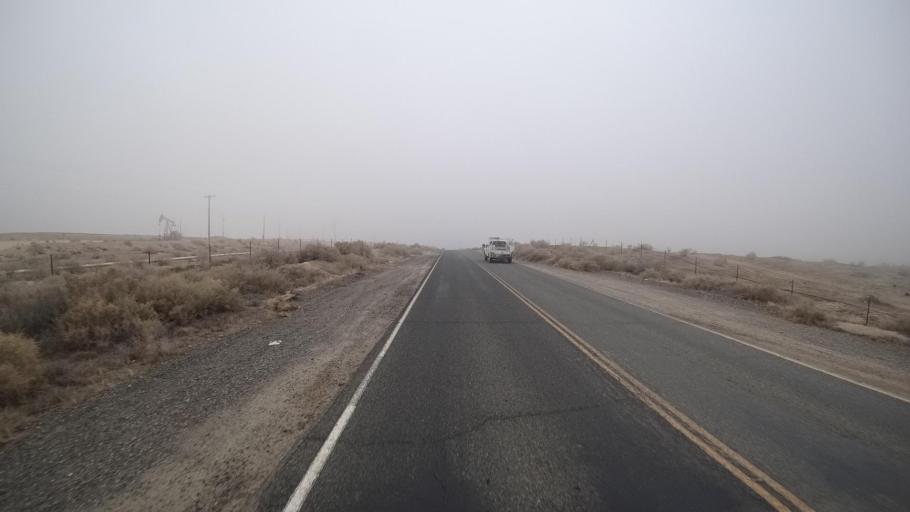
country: US
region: California
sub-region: Kern County
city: Ford City
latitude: 35.2747
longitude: -119.4677
